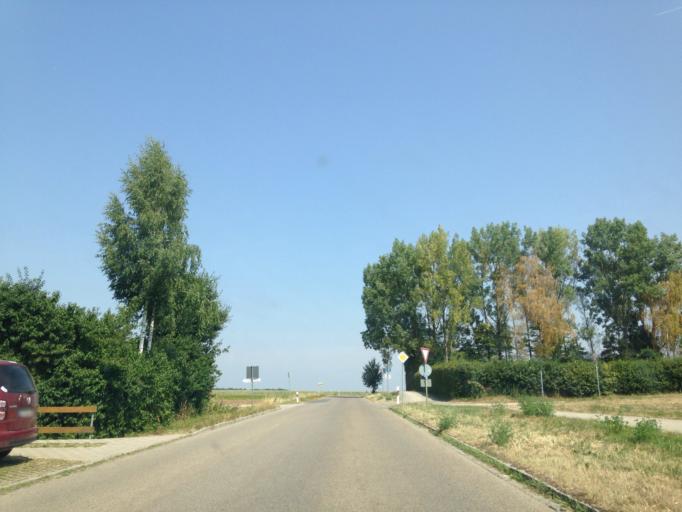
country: DE
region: Bavaria
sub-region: Regierungsbezirk Mittelfranken
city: Thalmassing
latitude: 49.1346
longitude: 11.2130
